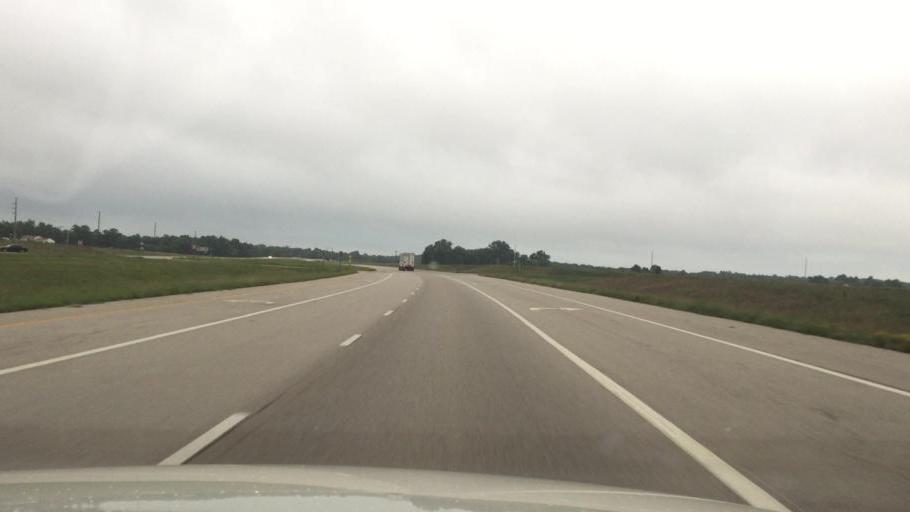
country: US
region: Kansas
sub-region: Montgomery County
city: Coffeyville
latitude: 37.0754
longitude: -95.5891
